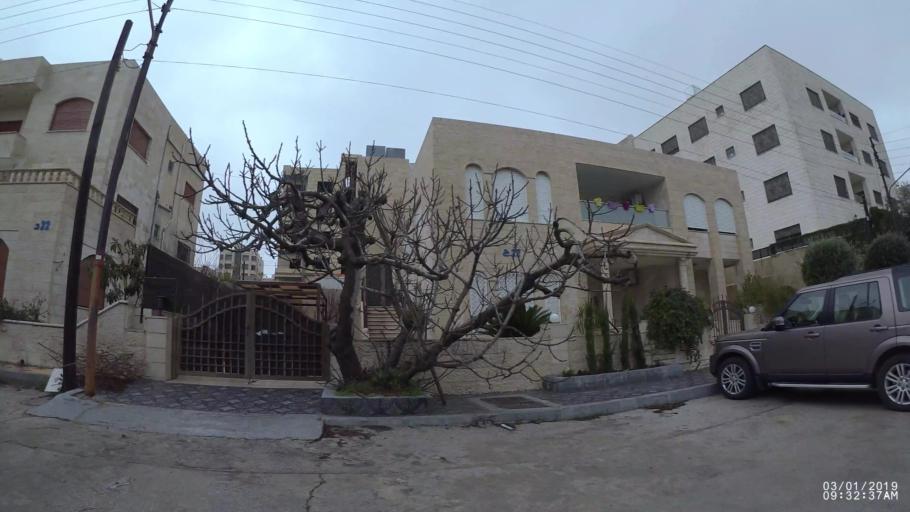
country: JO
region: Amman
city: Wadi as Sir
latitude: 31.9689
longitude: 35.8458
